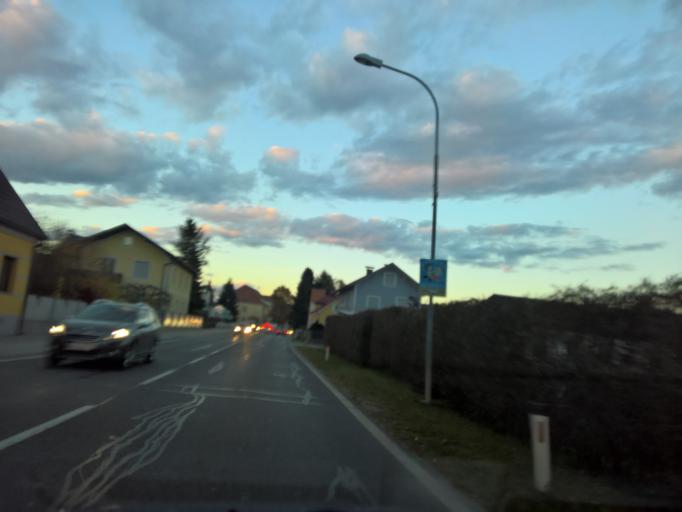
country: AT
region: Styria
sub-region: Politischer Bezirk Graz-Umgebung
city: Kalsdorf bei Graz
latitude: 46.9611
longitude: 15.4792
